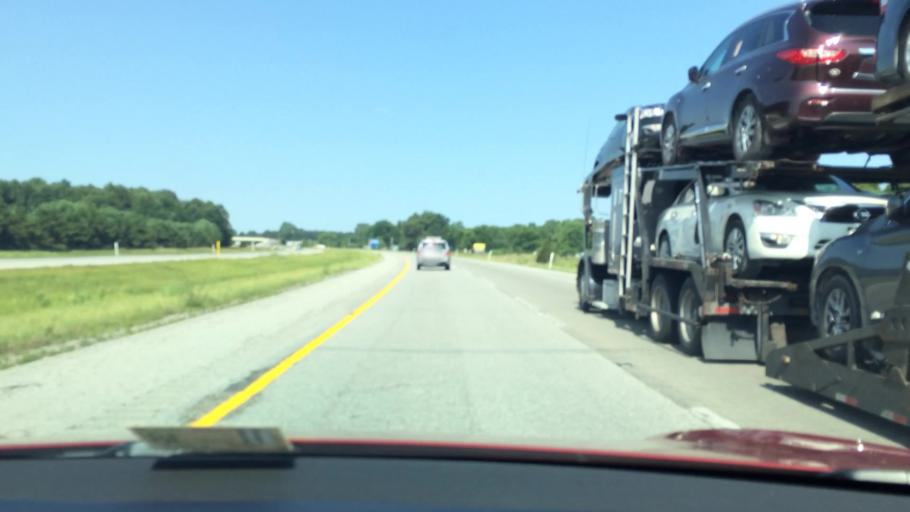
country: US
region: Michigan
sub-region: Saint Joseph County
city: White Pigeon
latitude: 41.7540
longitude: -85.6406
